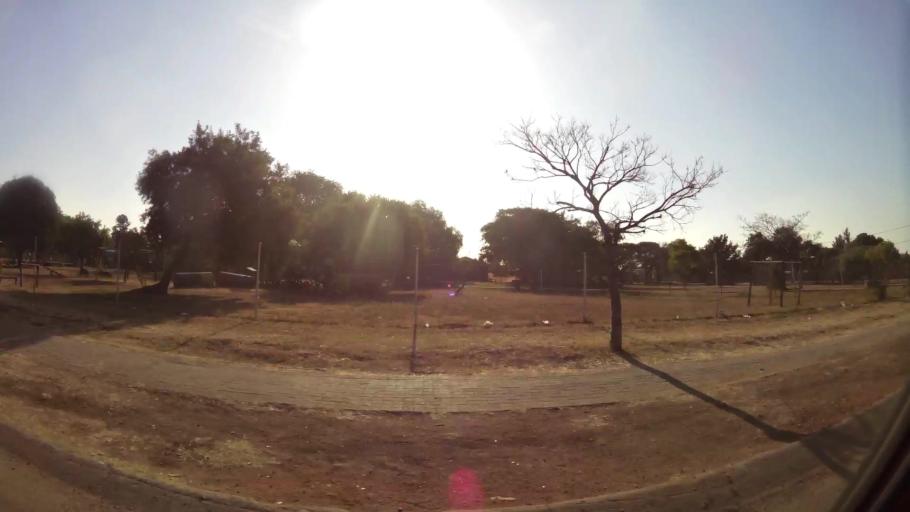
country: ZA
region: North-West
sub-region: Bojanala Platinum District Municipality
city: Rustenburg
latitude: -25.6458
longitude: 27.2423
